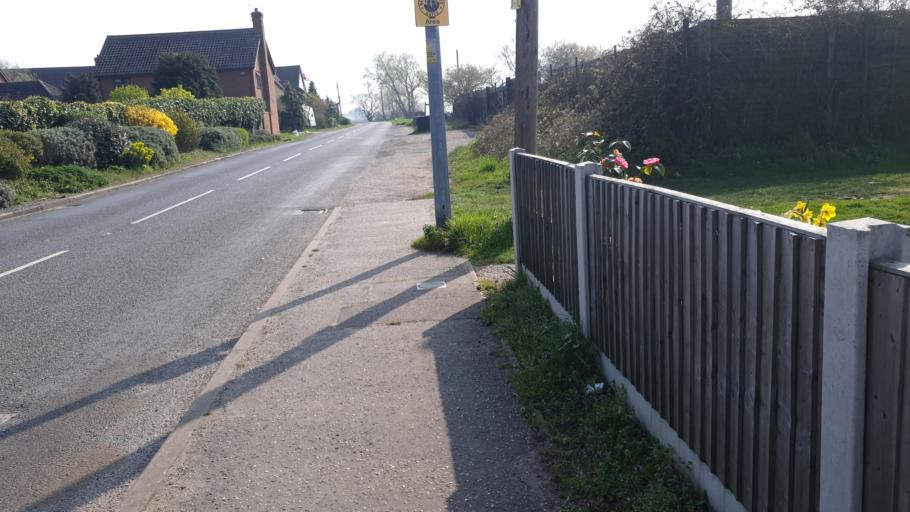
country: GB
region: England
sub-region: Essex
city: Mistley
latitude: 51.9110
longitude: 1.1429
